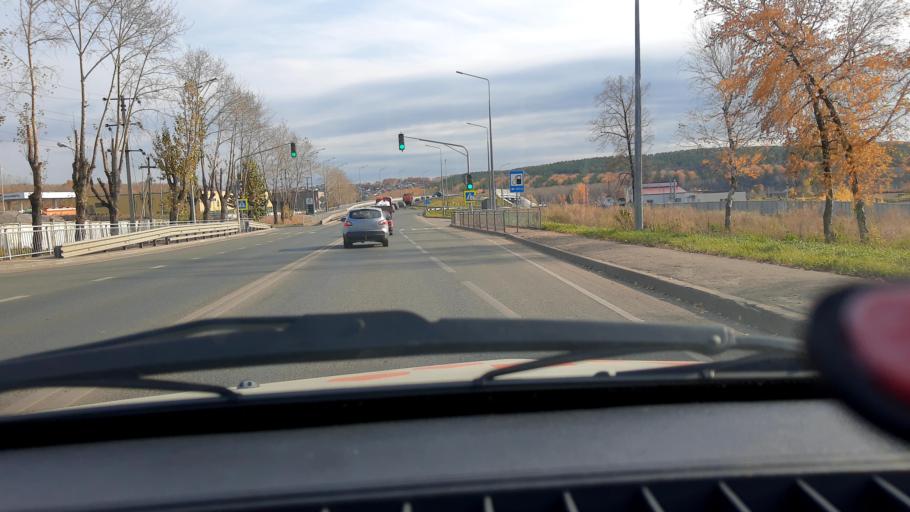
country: RU
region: Bashkortostan
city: Ufa
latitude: 54.8288
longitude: 56.1191
